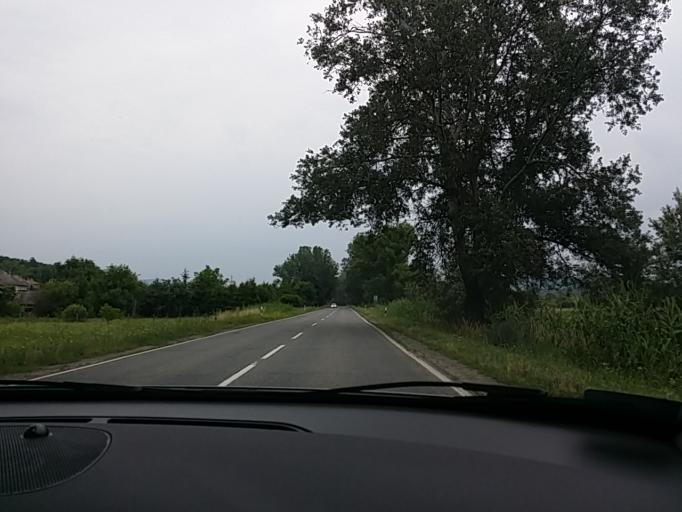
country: HU
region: Nograd
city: Batonyterenye
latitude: 47.9986
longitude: 19.8208
